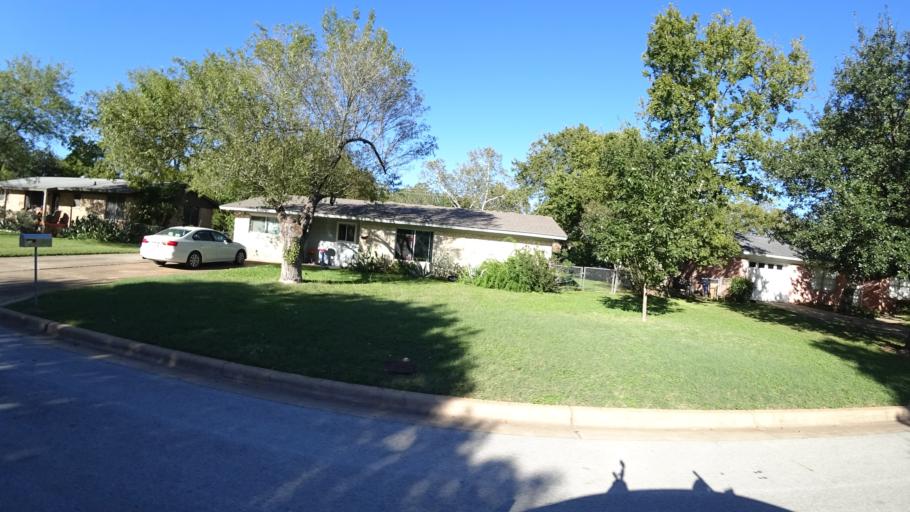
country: US
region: Texas
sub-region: Travis County
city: Rollingwood
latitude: 30.2356
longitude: -97.8093
